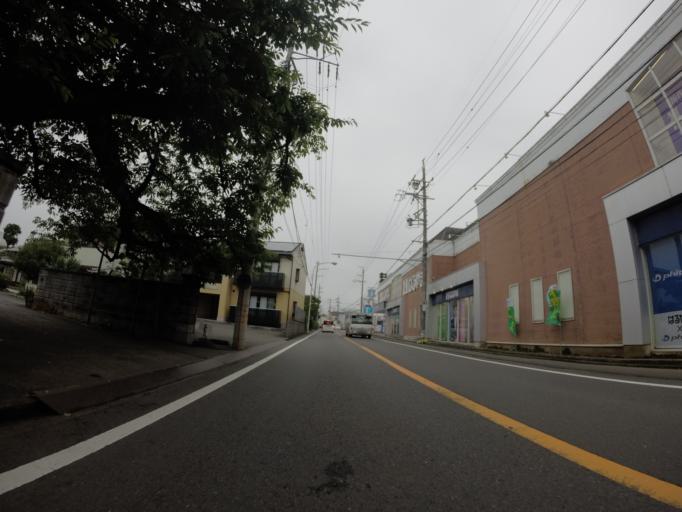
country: JP
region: Shizuoka
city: Shizuoka-shi
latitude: 34.9521
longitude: 138.3953
